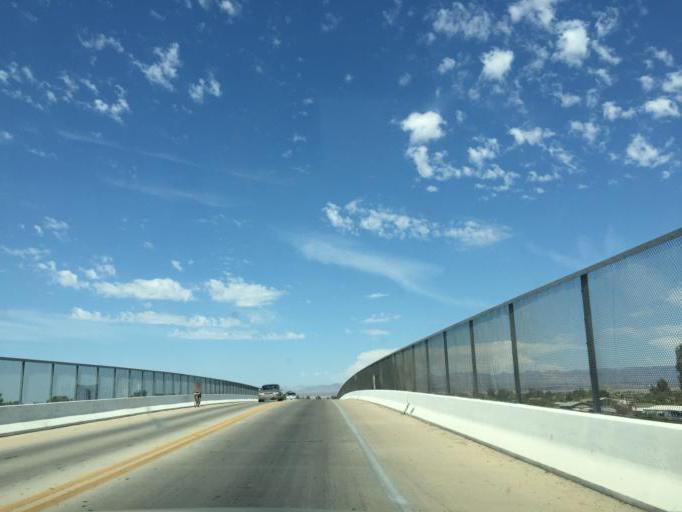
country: US
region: California
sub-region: San Bernardino County
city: Needles
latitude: 34.8512
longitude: -114.6094
